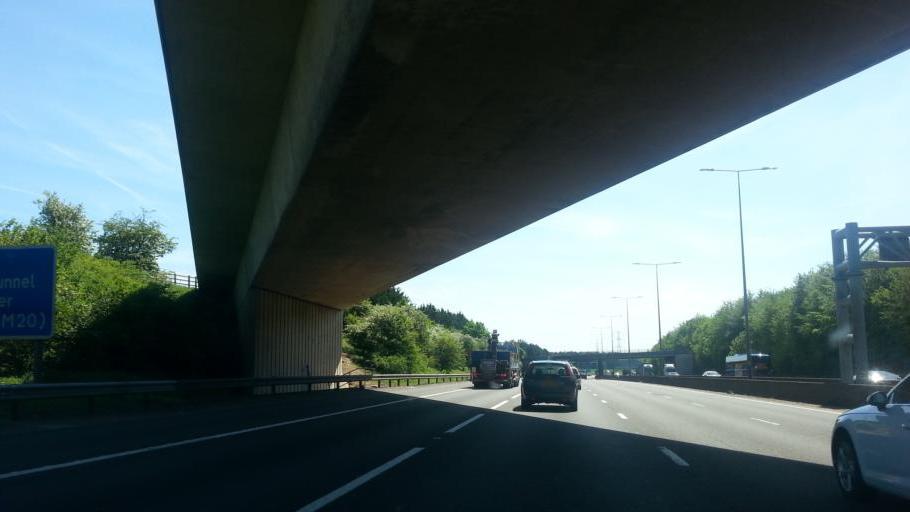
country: GB
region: England
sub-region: Hertfordshire
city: Abbots Langley
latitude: 51.7438
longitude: -0.4006
